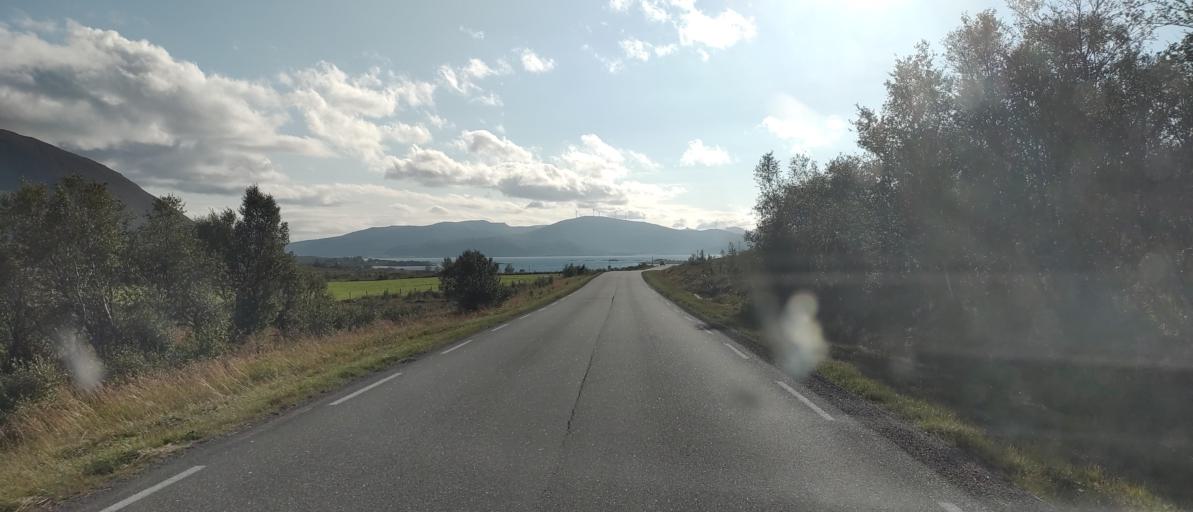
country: NO
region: Nordland
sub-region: Sortland
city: Sortland
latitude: 68.7903
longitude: 15.5017
